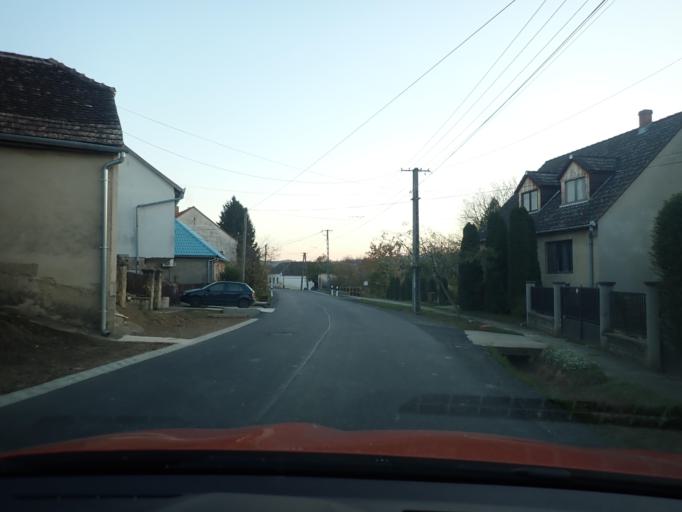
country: HU
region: Baranya
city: Kozarmisleny
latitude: 46.0372
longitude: 18.3875
